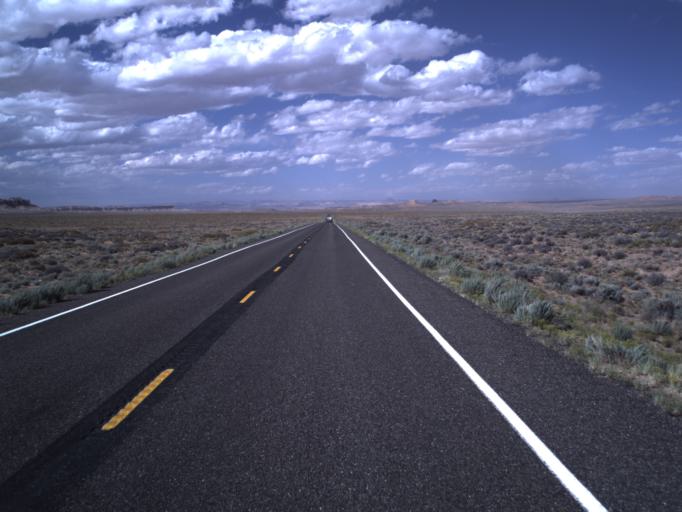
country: US
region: Utah
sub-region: Wayne County
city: Loa
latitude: 38.1684
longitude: -110.6236
